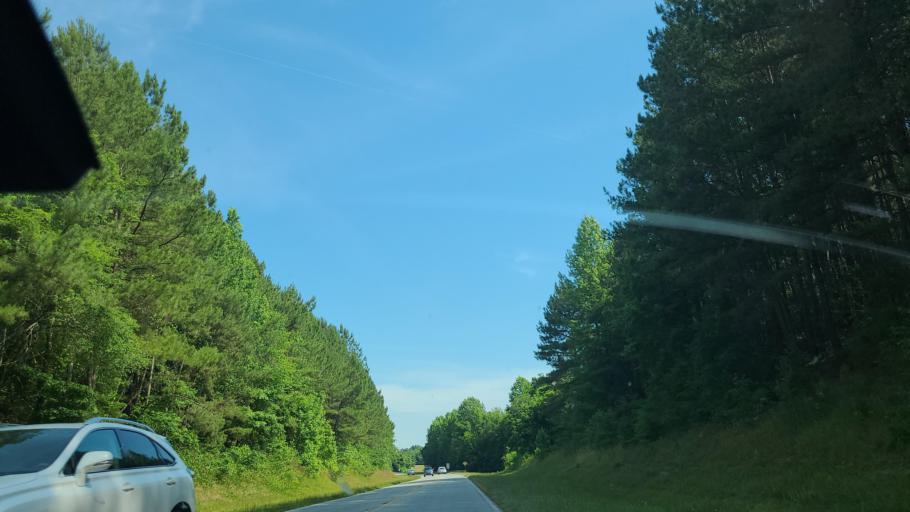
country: US
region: South Carolina
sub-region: Oconee County
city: Westminster
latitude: 34.6840
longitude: -83.0427
